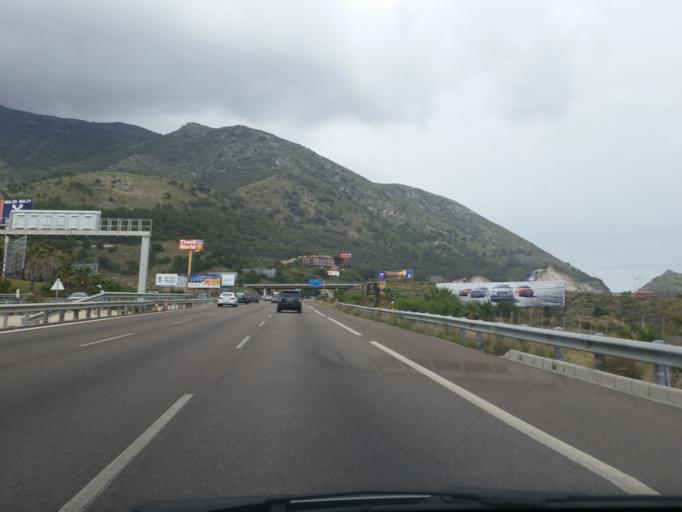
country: ES
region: Andalusia
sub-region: Provincia de Malaga
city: Mijas
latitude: 36.5823
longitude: -4.6056
